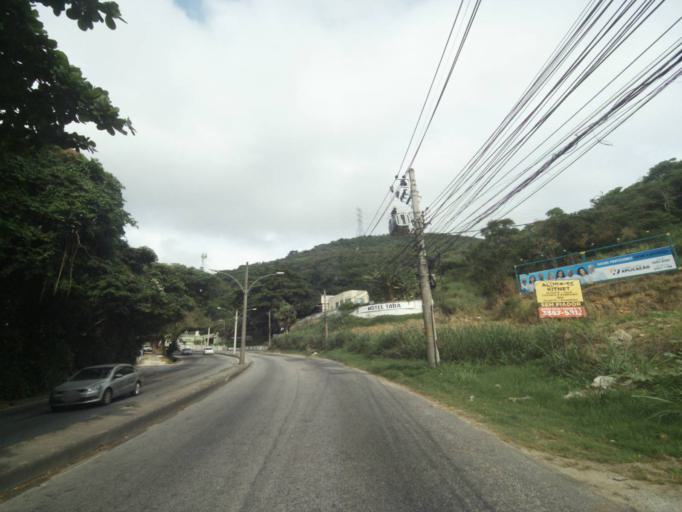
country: BR
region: Rio de Janeiro
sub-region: Nilopolis
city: Nilopolis
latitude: -22.8987
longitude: -43.3972
